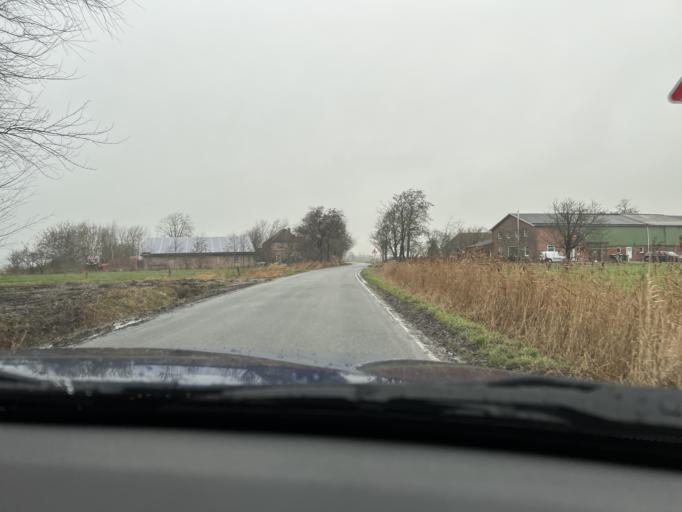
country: DE
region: Schleswig-Holstein
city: Lohe-Rickelshof
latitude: 54.2297
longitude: 9.0491
